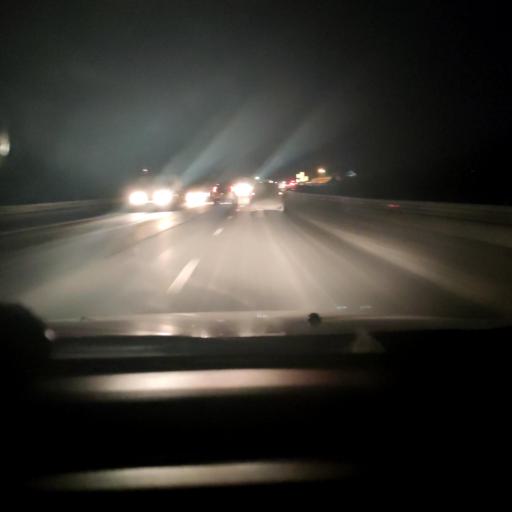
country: RU
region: Samara
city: Novokuybyshevsk
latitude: 53.0721
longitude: 50.0113
